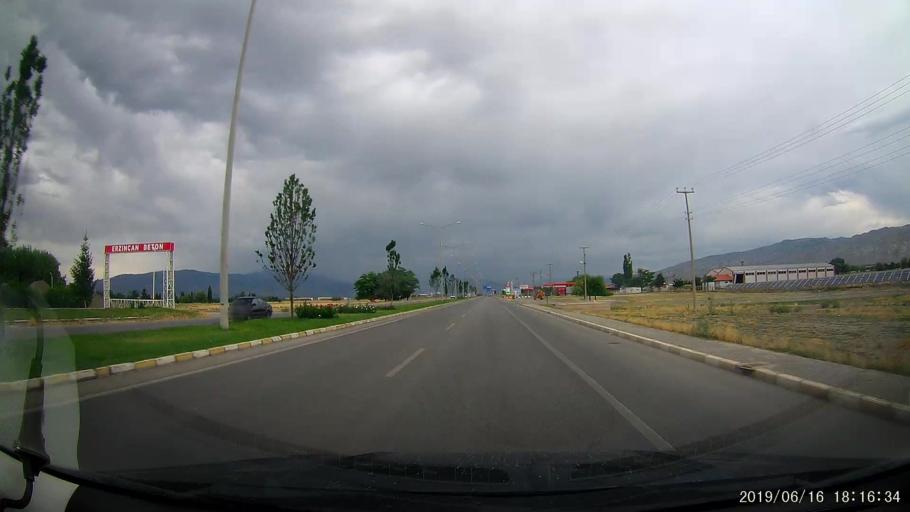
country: TR
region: Erzincan
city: Erzincan
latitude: 39.7291
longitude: 39.5462
